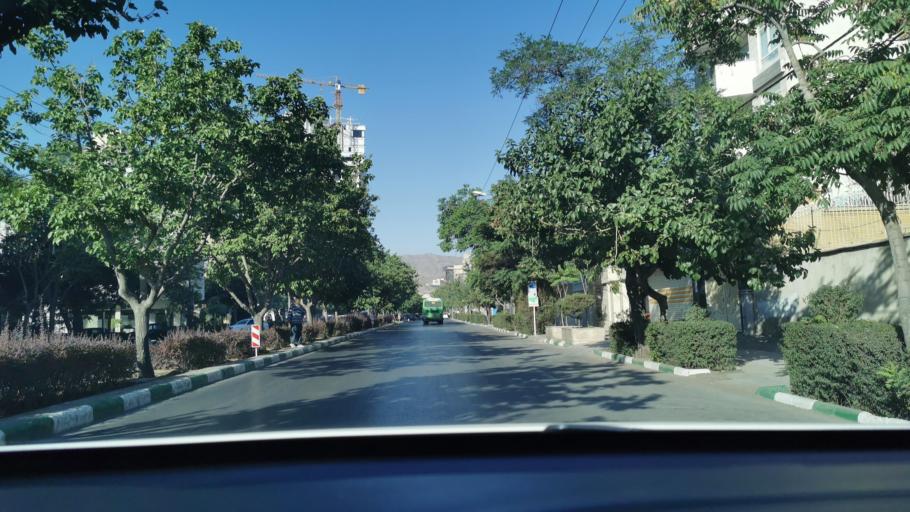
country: IR
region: Razavi Khorasan
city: Mashhad
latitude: 36.3164
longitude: 59.5203
